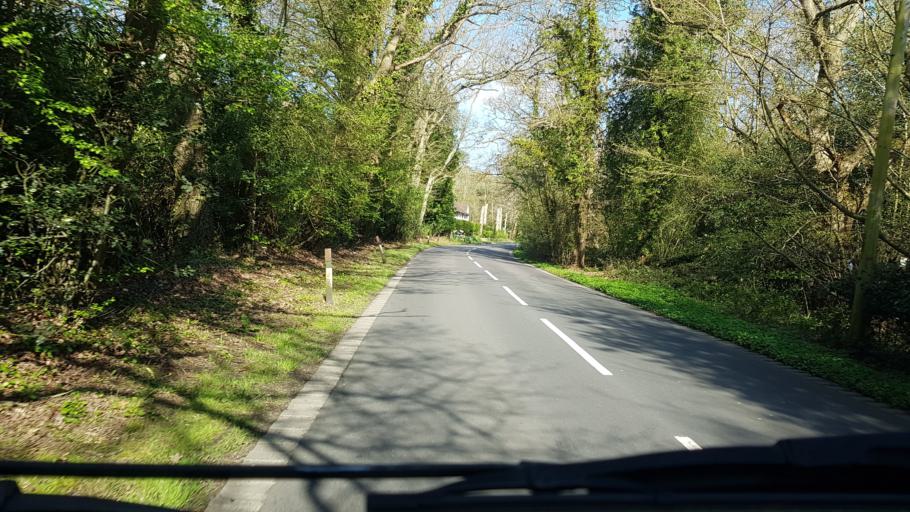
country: GB
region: England
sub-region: Surrey
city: Knaphill
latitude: 51.2960
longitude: -0.6033
